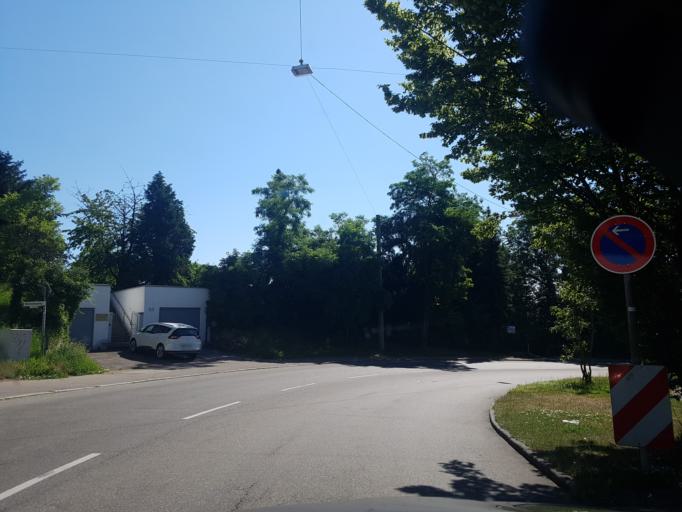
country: DE
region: Baden-Wuerttemberg
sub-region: Tuebingen Region
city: Ulm
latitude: 48.4126
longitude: 10.0060
